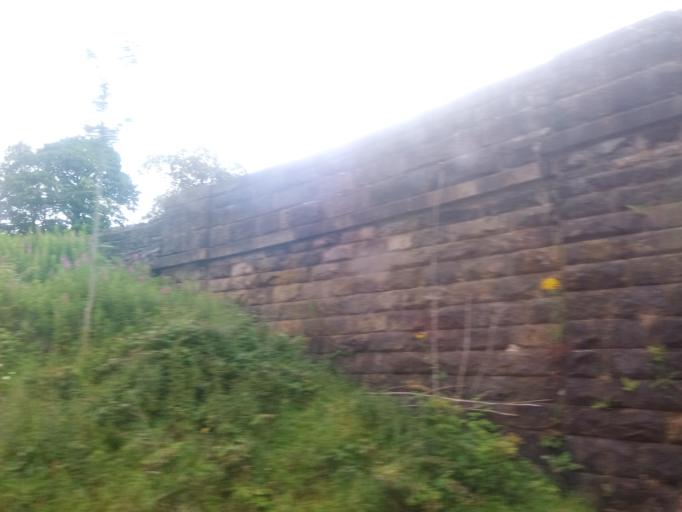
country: GB
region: England
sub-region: North Yorkshire
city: Settle
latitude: 54.0150
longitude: -2.2507
